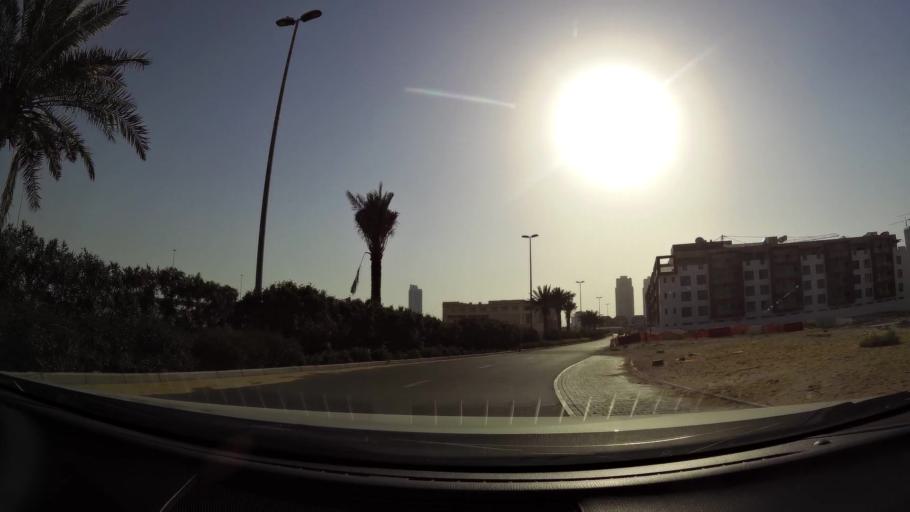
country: AE
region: Dubai
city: Dubai
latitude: 25.0458
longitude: 55.2047
